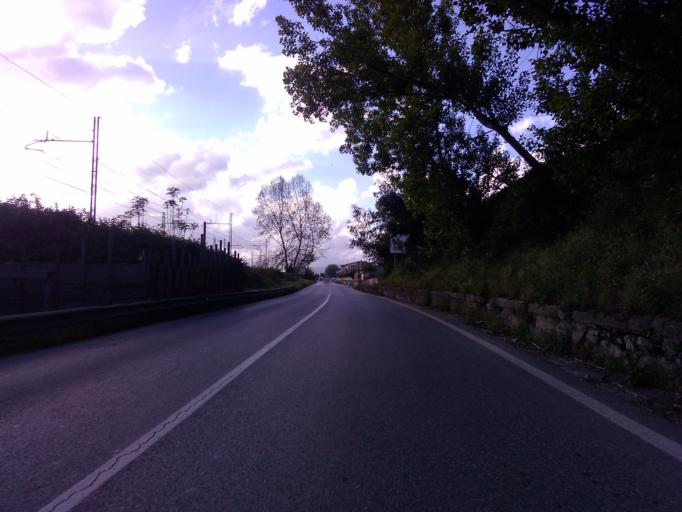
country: IT
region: Tuscany
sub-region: Provincia di Massa-Carrara
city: Capanne-Prato-Cinquale
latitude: 43.9979
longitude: 10.1721
